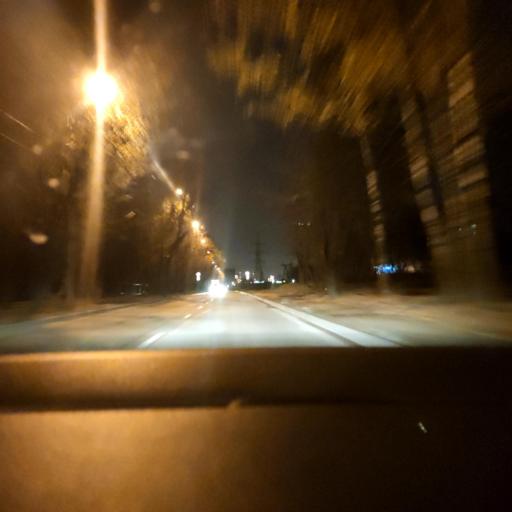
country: RU
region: Moscow
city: Kuz'minki
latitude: 55.6704
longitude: 37.8074
